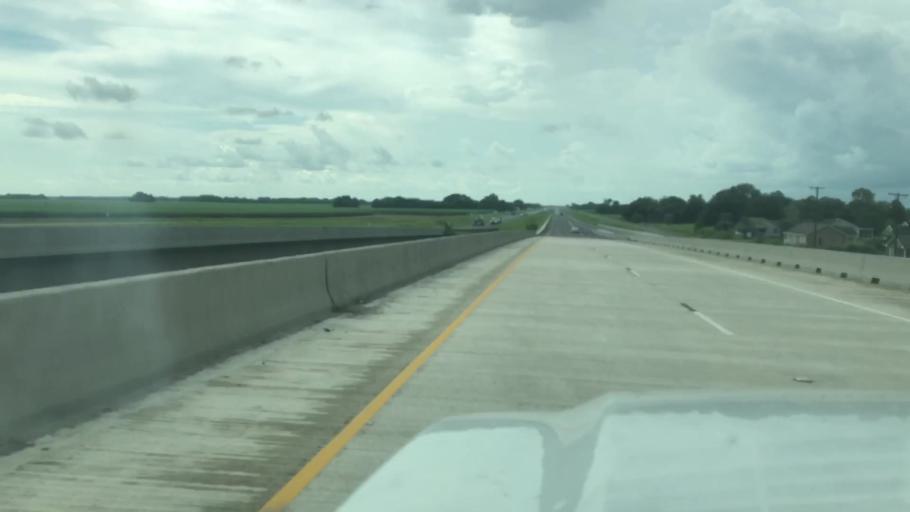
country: US
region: Louisiana
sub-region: Iberia Parish
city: Jeanerette
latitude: 29.8673
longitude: -91.6350
